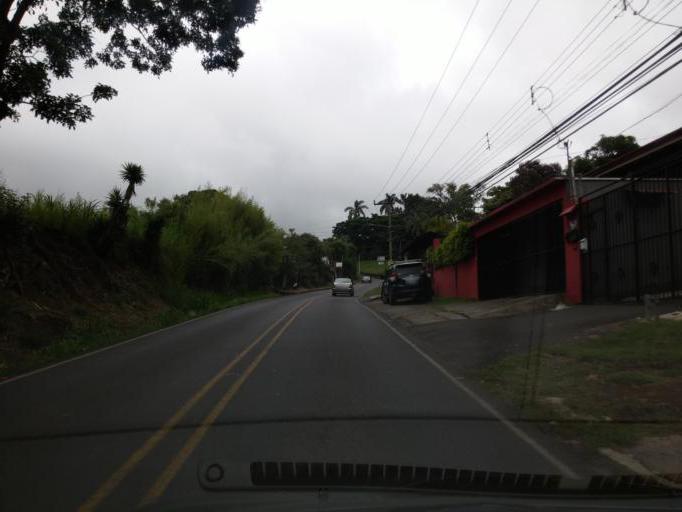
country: CR
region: Heredia
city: Mercedes
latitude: 10.0286
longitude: -84.1228
